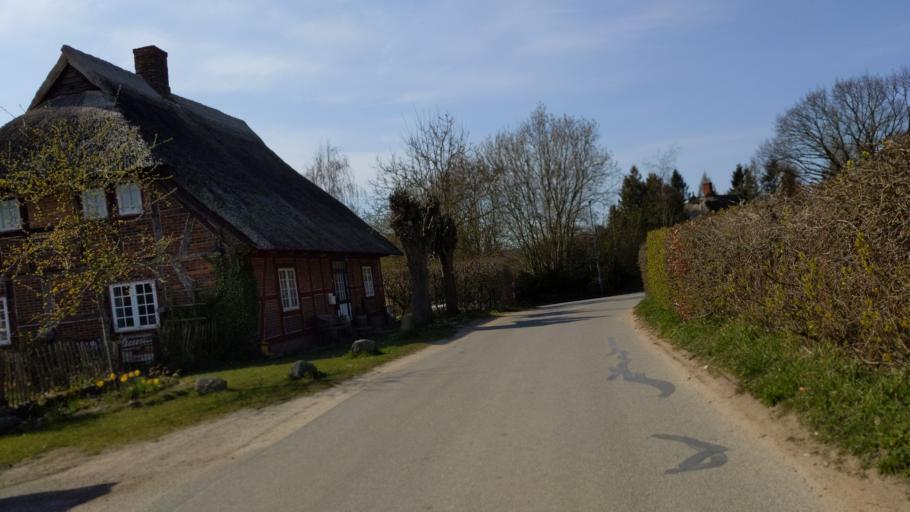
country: DE
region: Schleswig-Holstein
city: Schashagen
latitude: 54.1352
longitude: 10.8811
